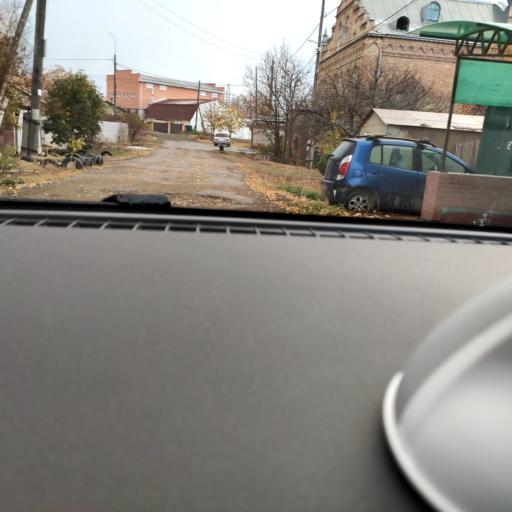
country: RU
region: Samara
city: Smyshlyayevka
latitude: 53.2376
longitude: 50.3187
